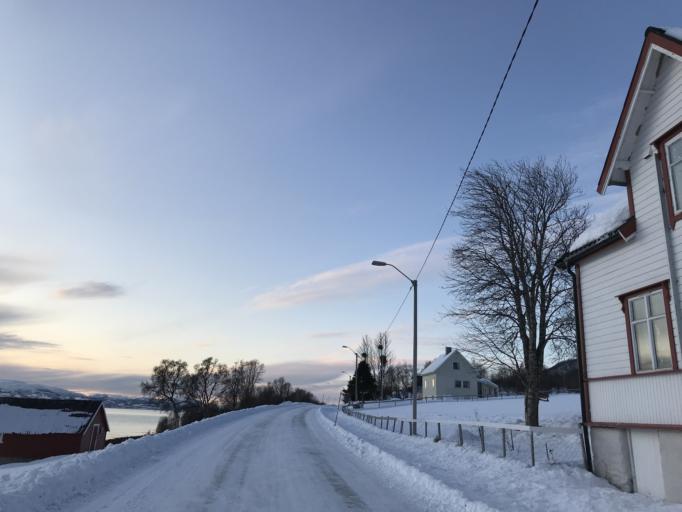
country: NO
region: Troms
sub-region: Karlsoy
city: Hansnes
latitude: 69.8470
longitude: 19.5395
